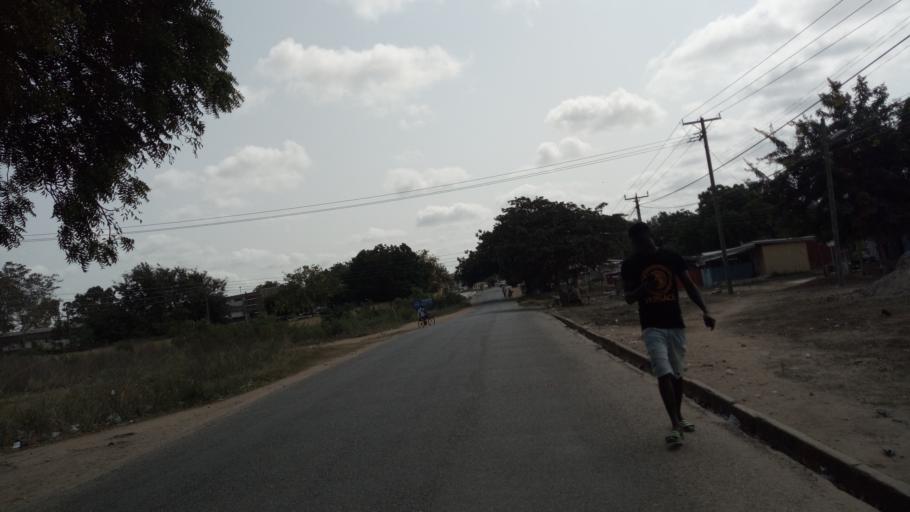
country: GH
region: Central
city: Winneba
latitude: 5.3700
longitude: -0.6436
